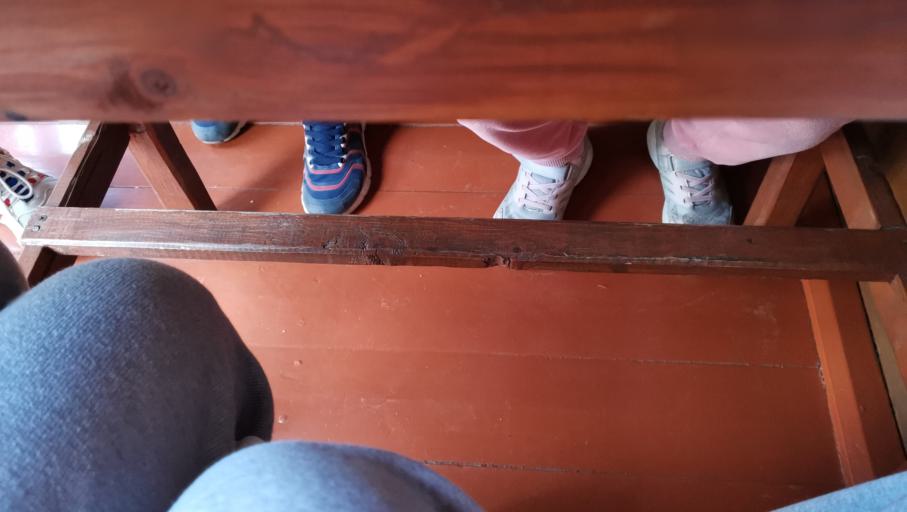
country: RU
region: Altay
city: Souzga
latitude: 51.9130
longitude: 85.8550
